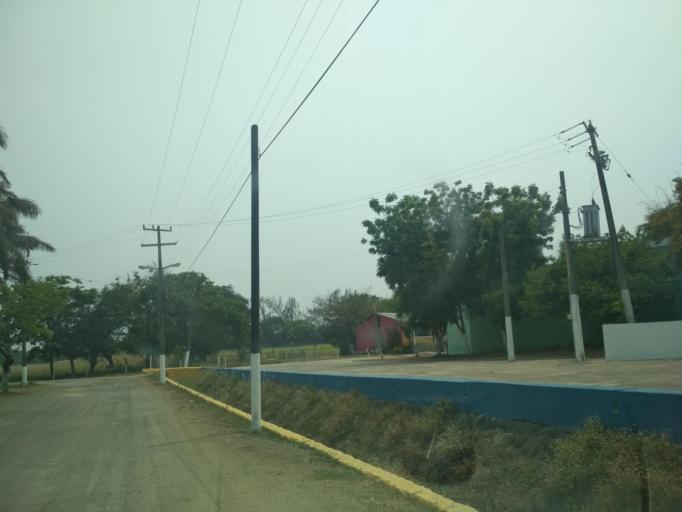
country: MX
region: Veracruz
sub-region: Veracruz
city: Las Amapolas
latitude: 19.1640
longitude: -96.2084
